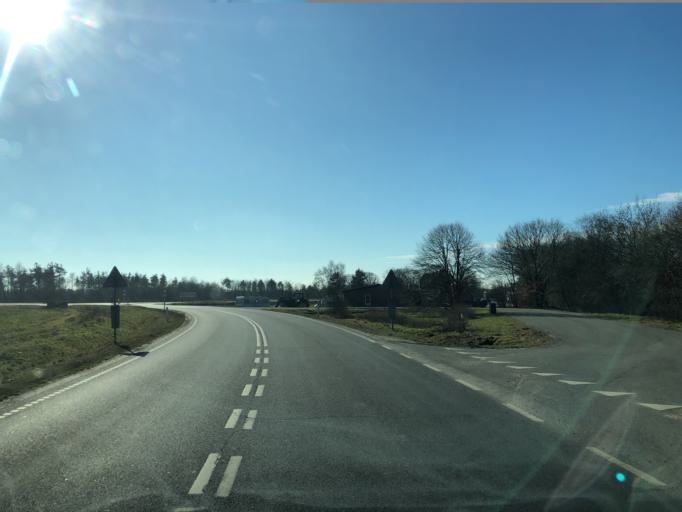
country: DK
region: Central Jutland
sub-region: Ikast-Brande Kommune
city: Bording Kirkeby
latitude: 56.1449
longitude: 9.2159
